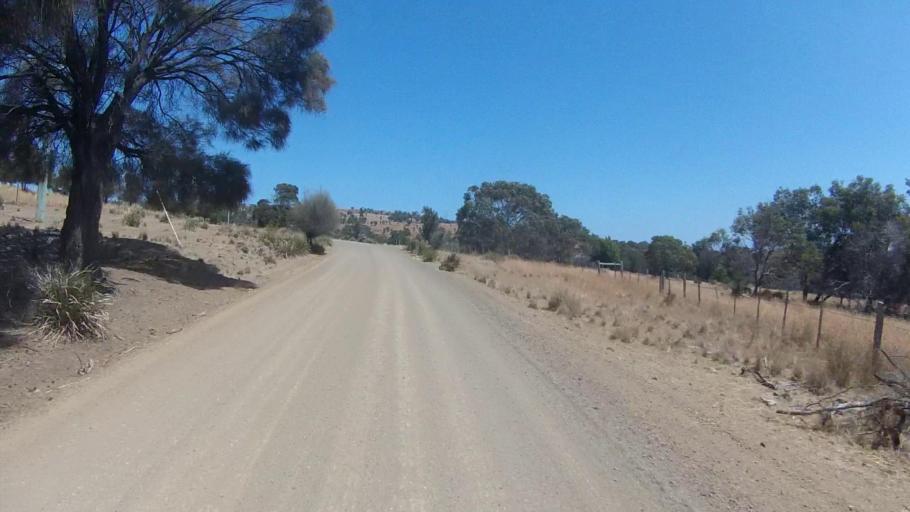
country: AU
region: Tasmania
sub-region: Sorell
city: Sorell
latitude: -42.8930
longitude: 147.8422
